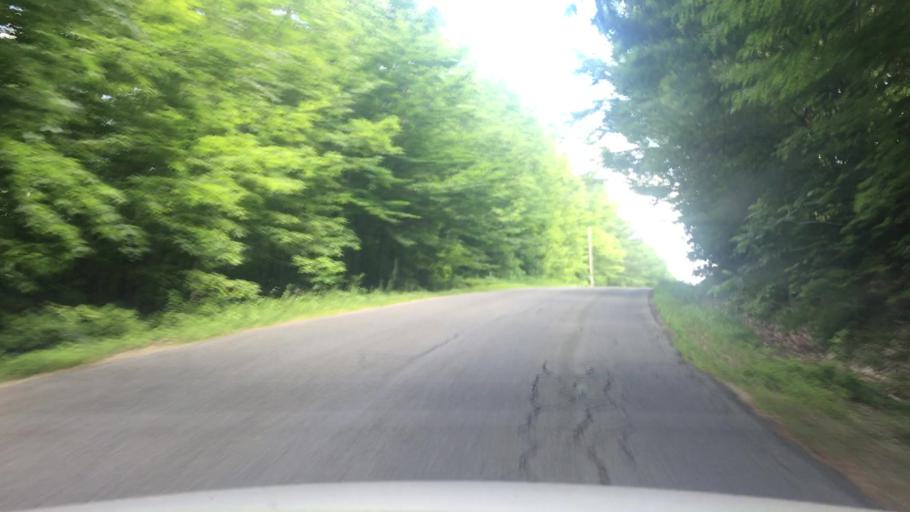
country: US
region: Maine
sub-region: Franklin County
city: Wilton
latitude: 44.6254
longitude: -70.2308
